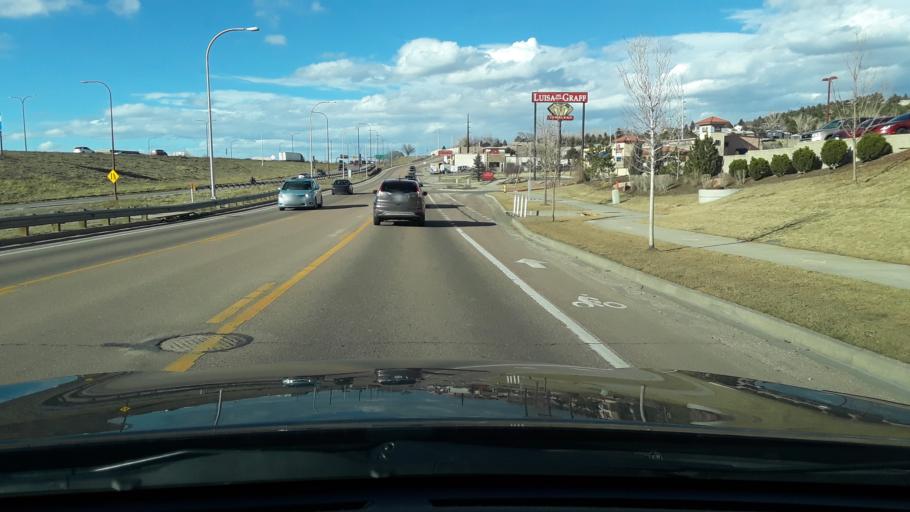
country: US
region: Colorado
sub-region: El Paso County
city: Colorado Springs
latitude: 38.9155
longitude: -104.8152
